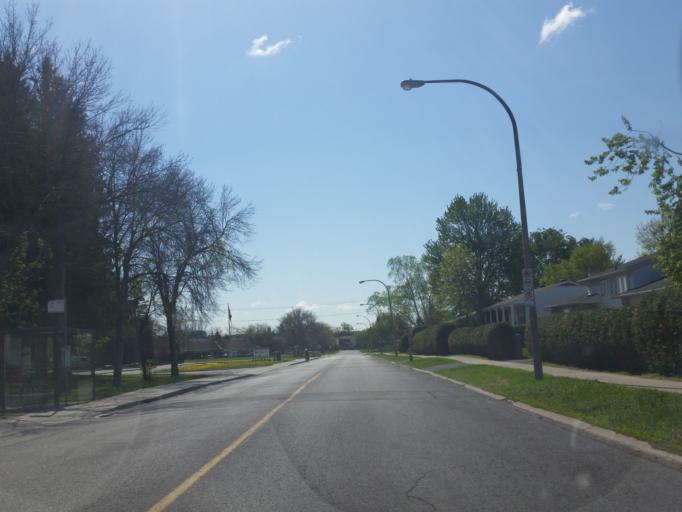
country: CA
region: Ontario
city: Ottawa
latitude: 45.3501
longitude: -75.7184
